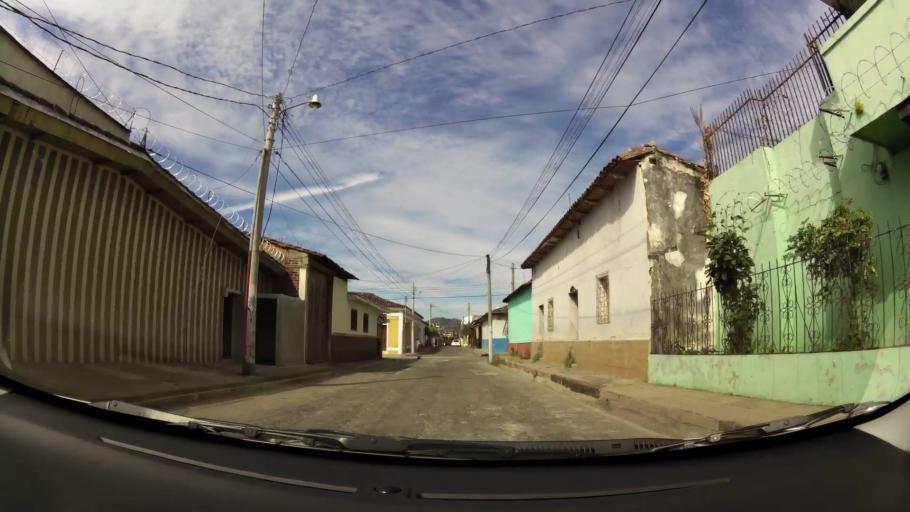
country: SV
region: Santa Ana
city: Chalchuapa
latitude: 13.9826
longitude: -89.6781
